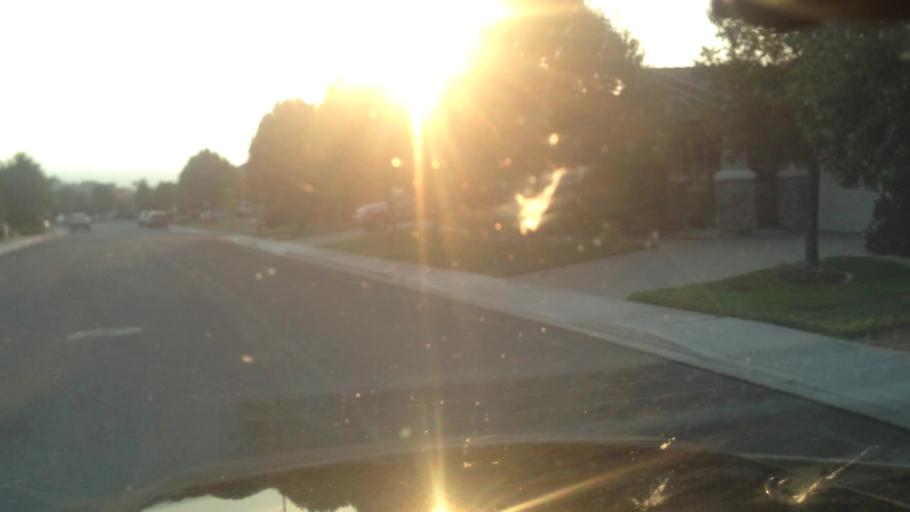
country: US
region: Nevada
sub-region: Washoe County
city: Sparks
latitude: 39.4086
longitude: -119.7372
